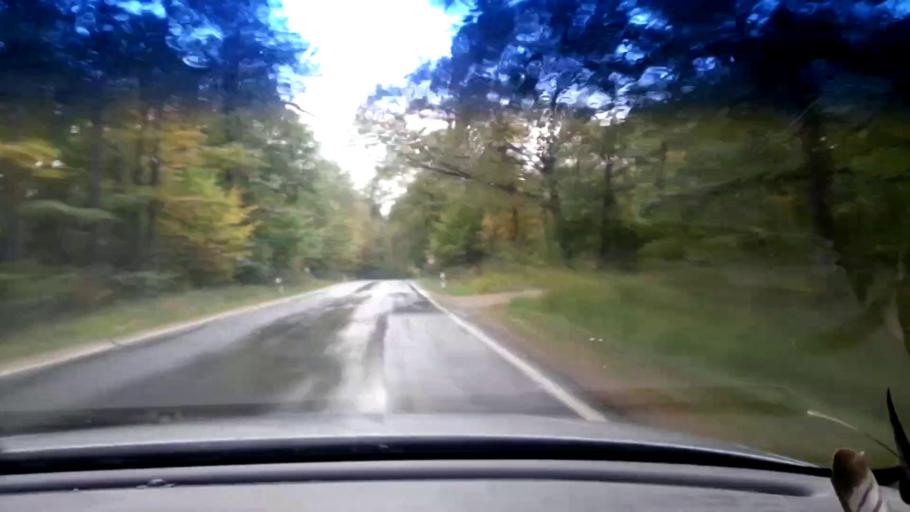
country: DE
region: Bavaria
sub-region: Upper Franconia
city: Walsdorf
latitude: 49.8663
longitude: 10.7512
